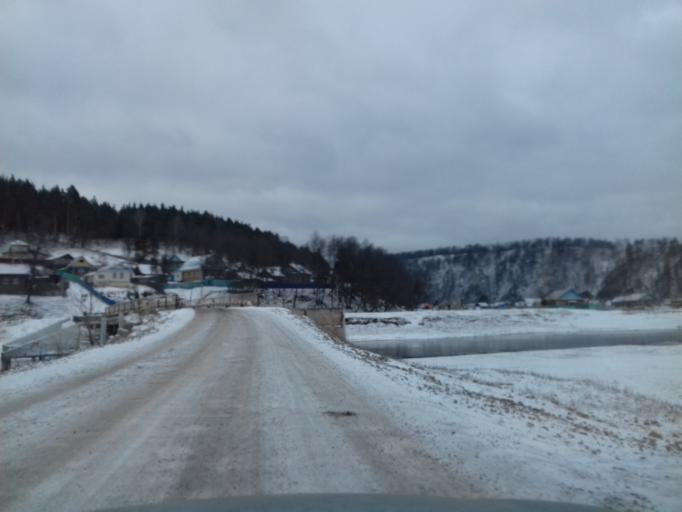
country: RU
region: Bashkortostan
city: Starosubkhangulovo
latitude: 53.0953
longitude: 57.4290
